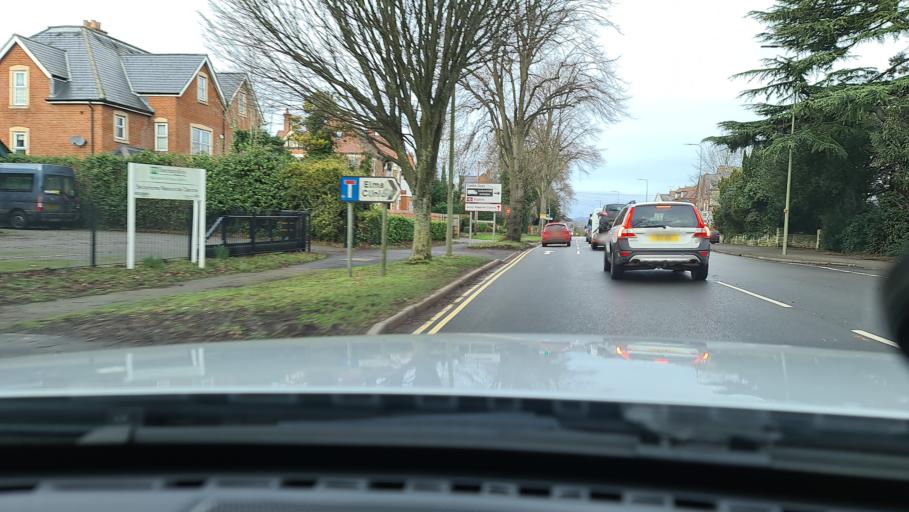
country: GB
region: England
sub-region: Oxfordshire
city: Banbury
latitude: 52.0542
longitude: -1.3386
